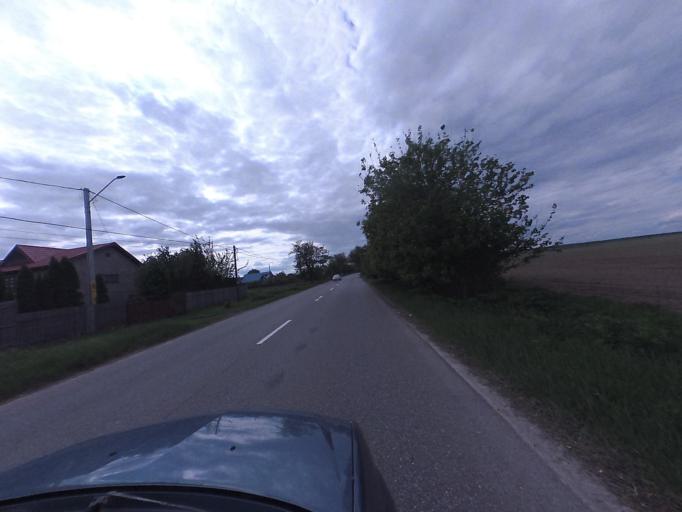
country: RO
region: Neamt
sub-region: Comuna Trifesti
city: Miron Costin
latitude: 46.9575
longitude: 26.8033
